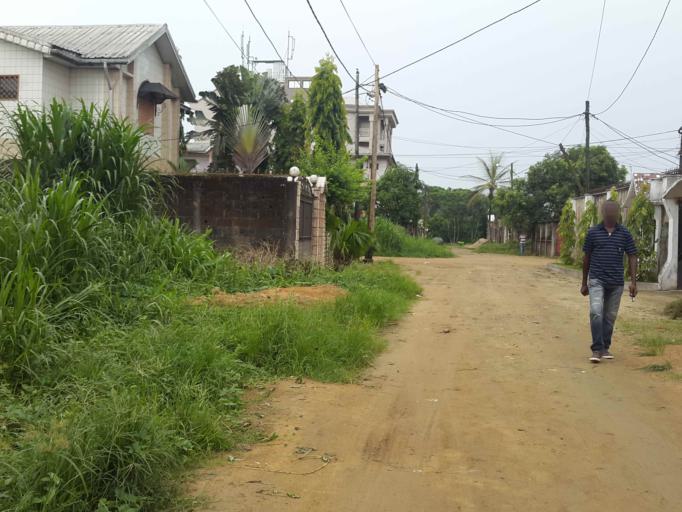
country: CM
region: Littoral
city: Douala
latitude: 4.0929
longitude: 9.7295
